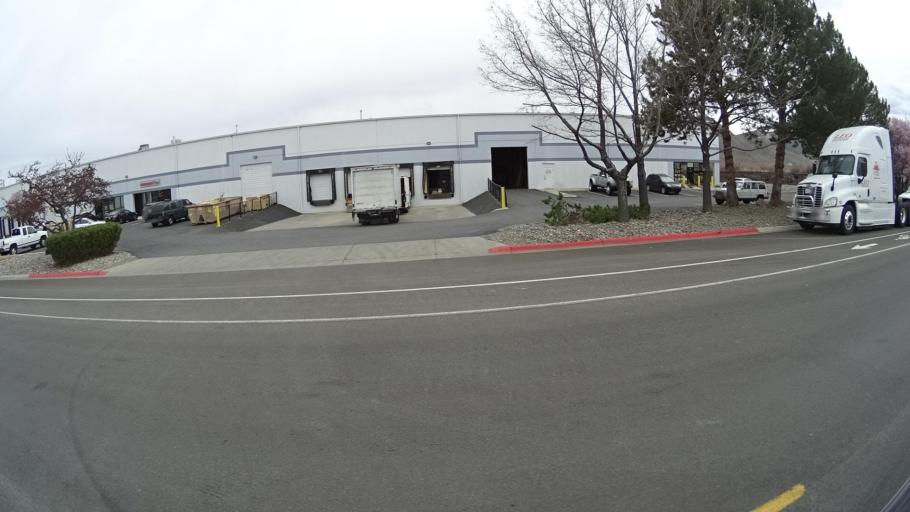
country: US
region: Nevada
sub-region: Washoe County
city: Sparks
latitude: 39.5154
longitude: -119.7301
